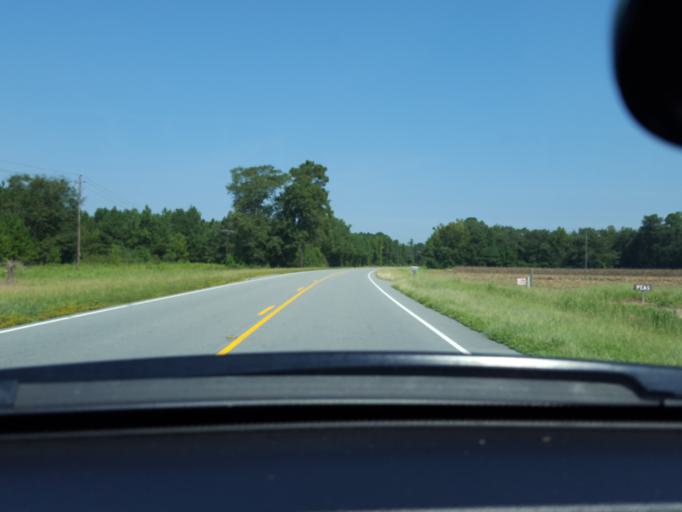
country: US
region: North Carolina
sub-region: Bladen County
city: Elizabethtown
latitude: 34.6798
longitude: -78.4900
